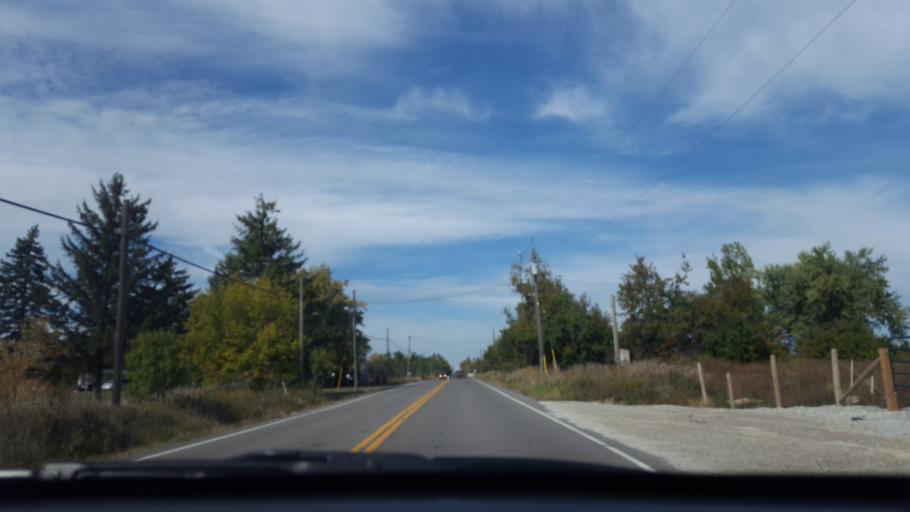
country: CA
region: Ontario
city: Vaughan
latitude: 43.8534
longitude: -79.5895
